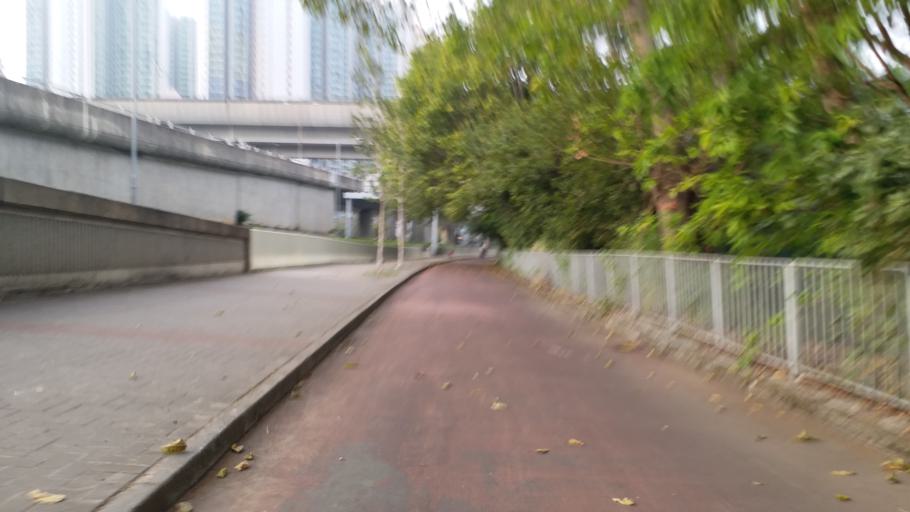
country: HK
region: Yuen Long
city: Yuen Long Kau Hui
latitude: 22.4503
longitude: 114.0097
